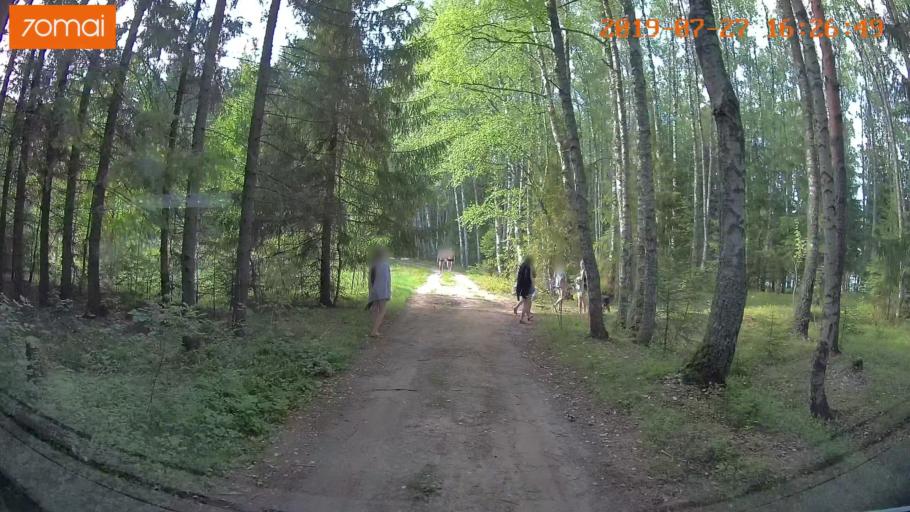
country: RU
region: Ivanovo
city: Novo-Talitsy
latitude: 57.0918
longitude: 40.8539
